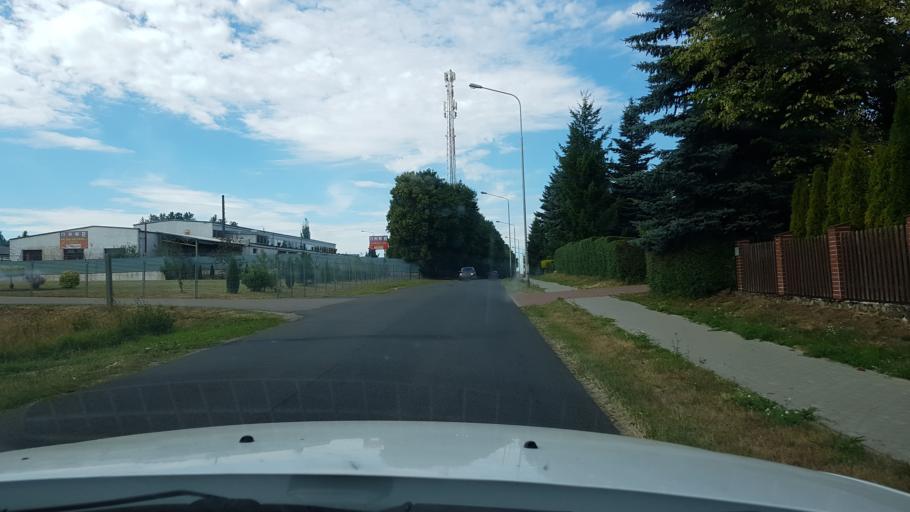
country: PL
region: West Pomeranian Voivodeship
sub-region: Powiat drawski
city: Zlocieniec
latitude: 53.5217
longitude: 16.0170
